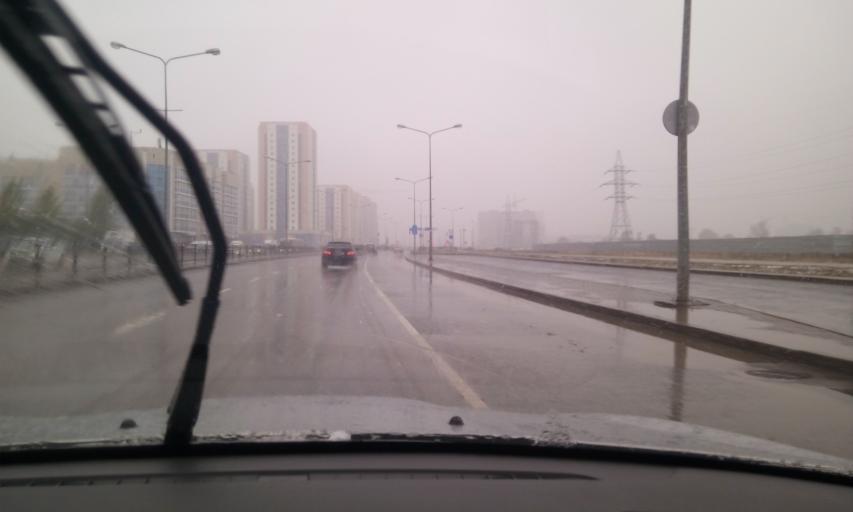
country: KZ
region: Astana Qalasy
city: Astana
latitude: 51.1472
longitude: 71.3721
